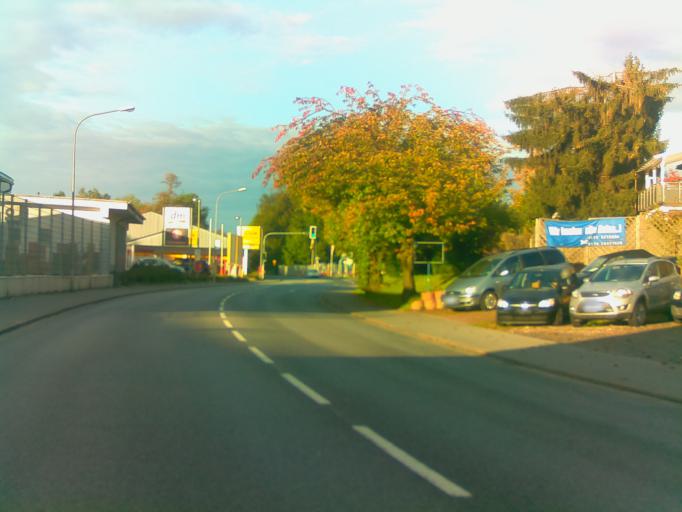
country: DE
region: Hesse
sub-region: Regierungsbezirk Darmstadt
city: Furth
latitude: 49.6557
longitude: 8.7865
